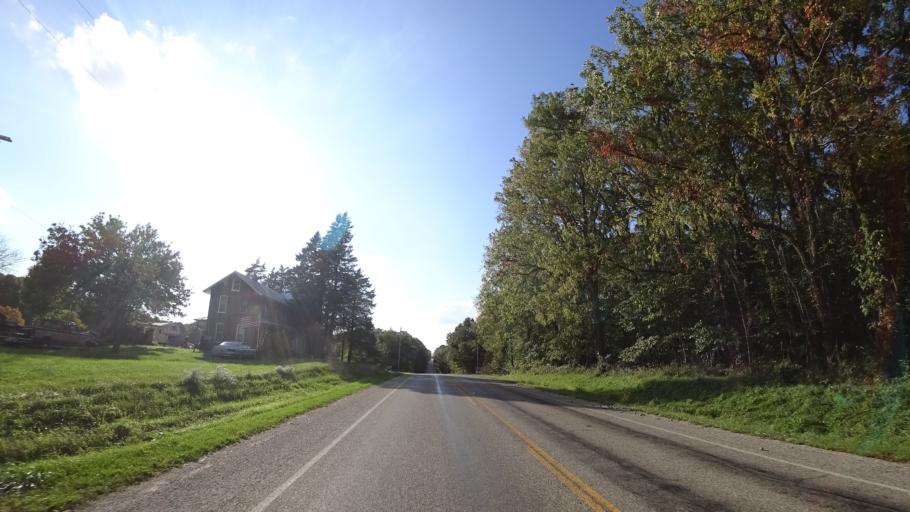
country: US
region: Michigan
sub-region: Saint Joseph County
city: Centreville
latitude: 41.8535
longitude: -85.4935
